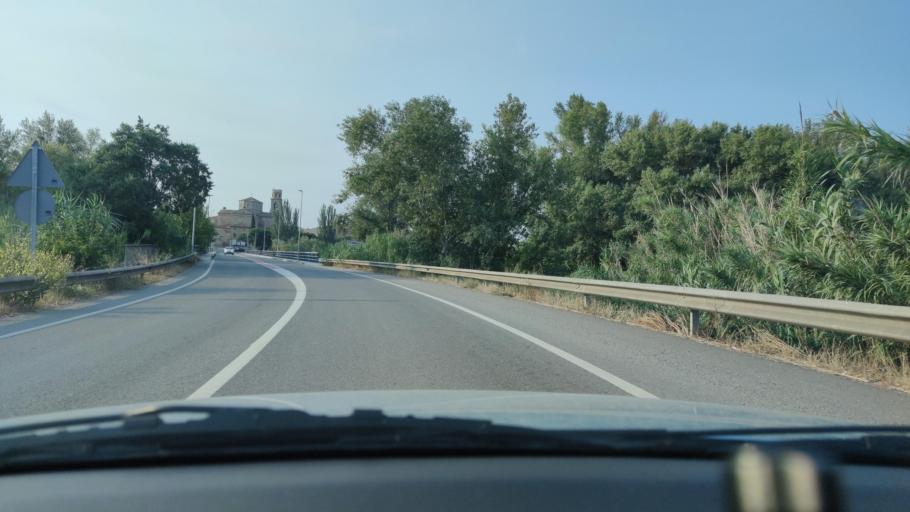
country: ES
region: Catalonia
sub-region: Provincia de Lleida
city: Torres de Segre
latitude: 41.5378
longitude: 0.5113
